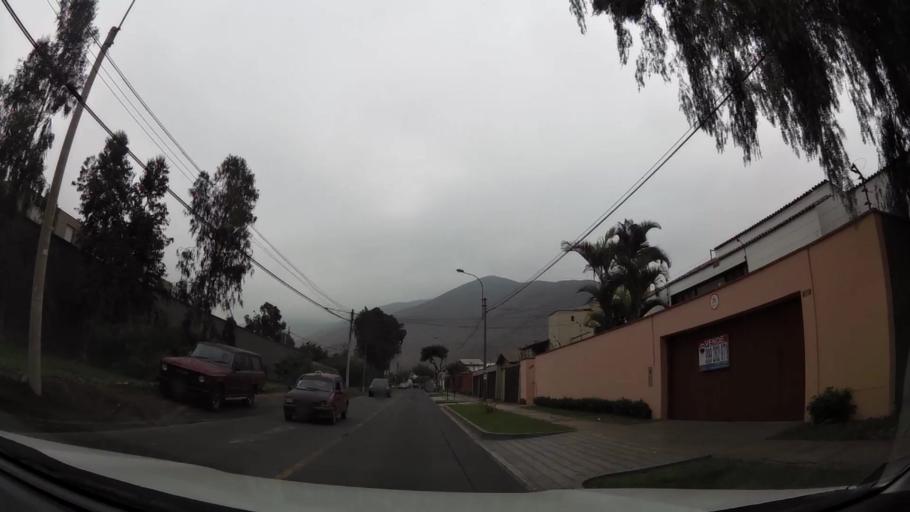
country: PE
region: Lima
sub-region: Lima
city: La Molina
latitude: -12.0804
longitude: -76.9152
